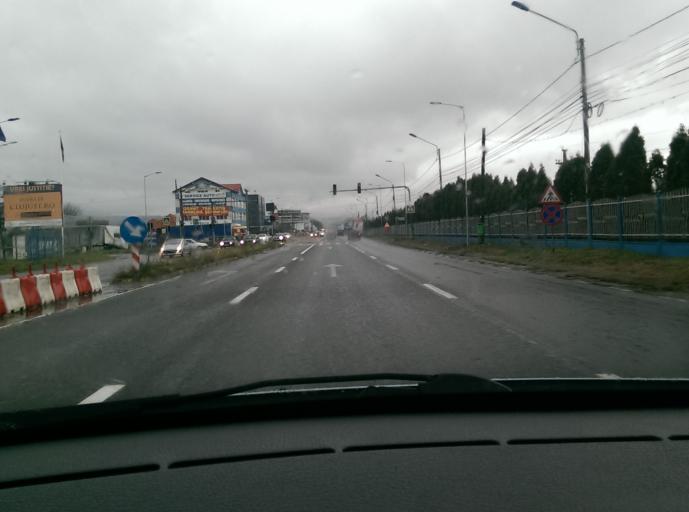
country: RO
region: Cluj
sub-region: Comuna Floresti
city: Floresti
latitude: 46.7526
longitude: 23.5258
